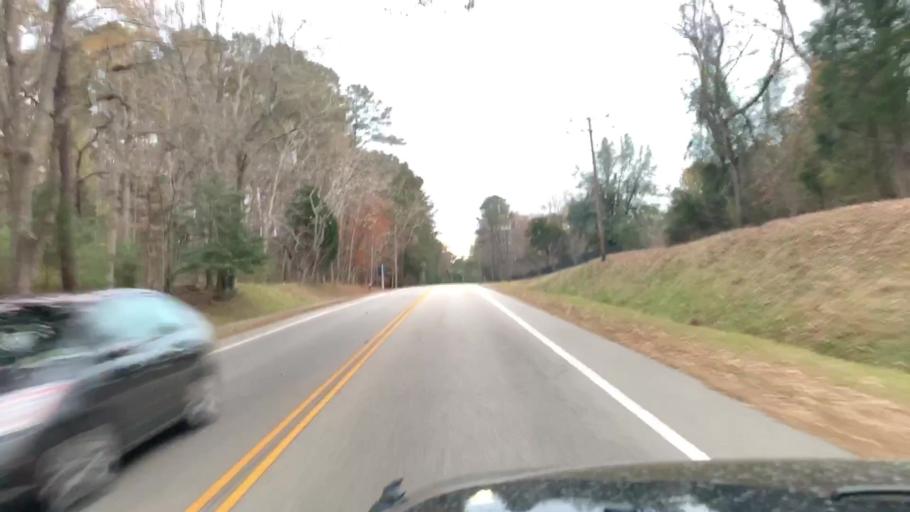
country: US
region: Virginia
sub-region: City of Williamsburg
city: Williamsburg
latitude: 37.2549
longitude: -76.7104
